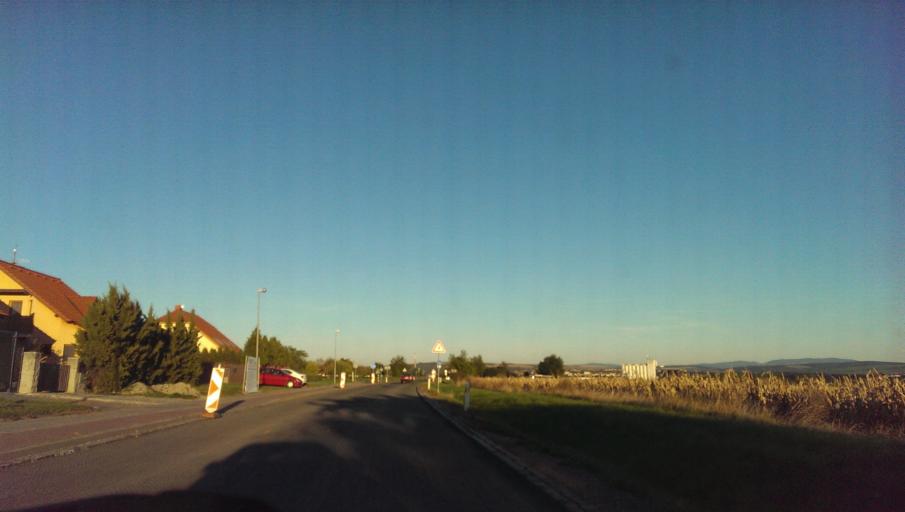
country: CZ
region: Zlin
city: Zlechov
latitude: 49.0741
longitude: 17.3970
